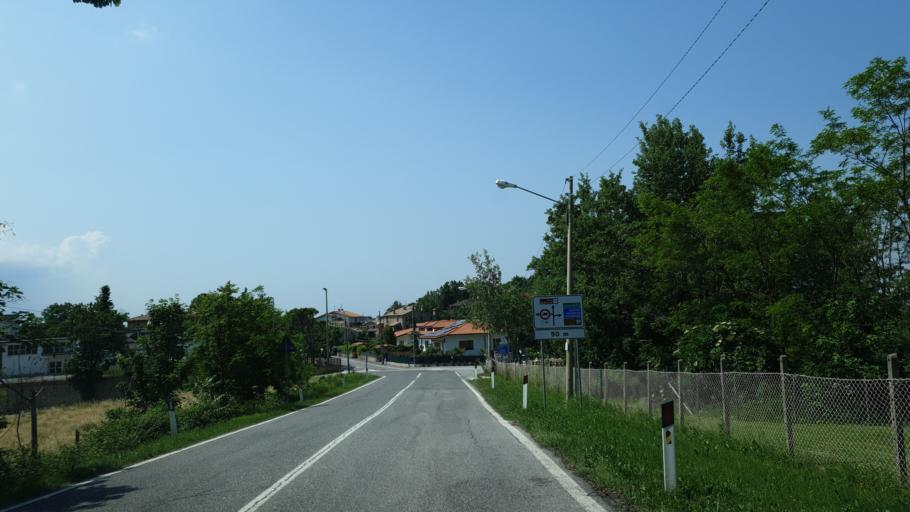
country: SM
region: San Marino
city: San Marino
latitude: 43.9369
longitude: 12.4341
